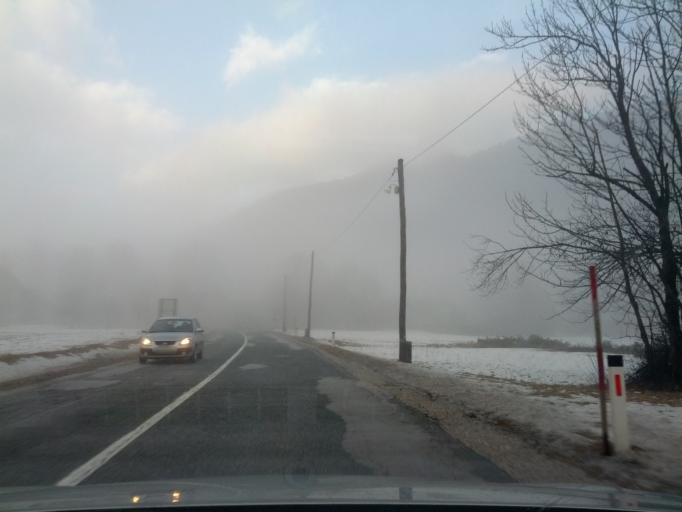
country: SI
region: Kranjska Gora
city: Mojstrana
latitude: 46.4832
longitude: 13.8486
